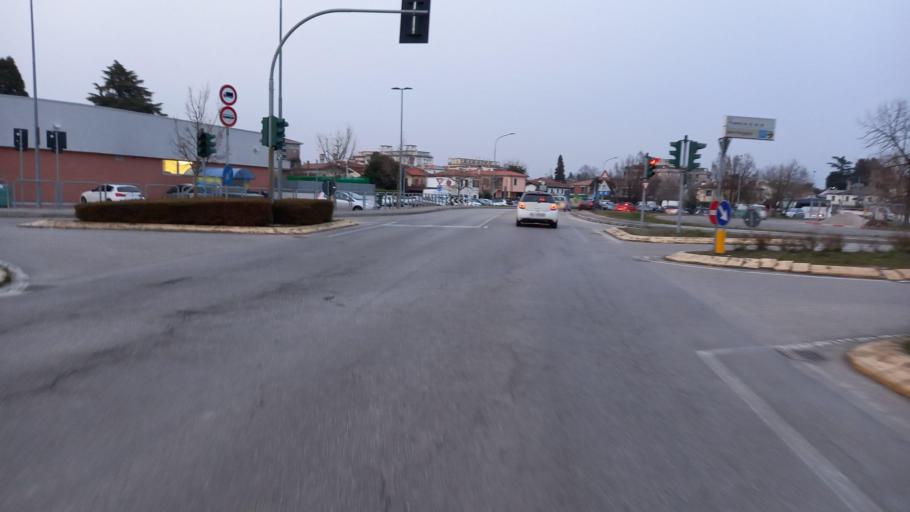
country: IT
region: Veneto
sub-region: Provincia di Treviso
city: Mogliano Veneto
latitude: 45.5585
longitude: 12.2301
